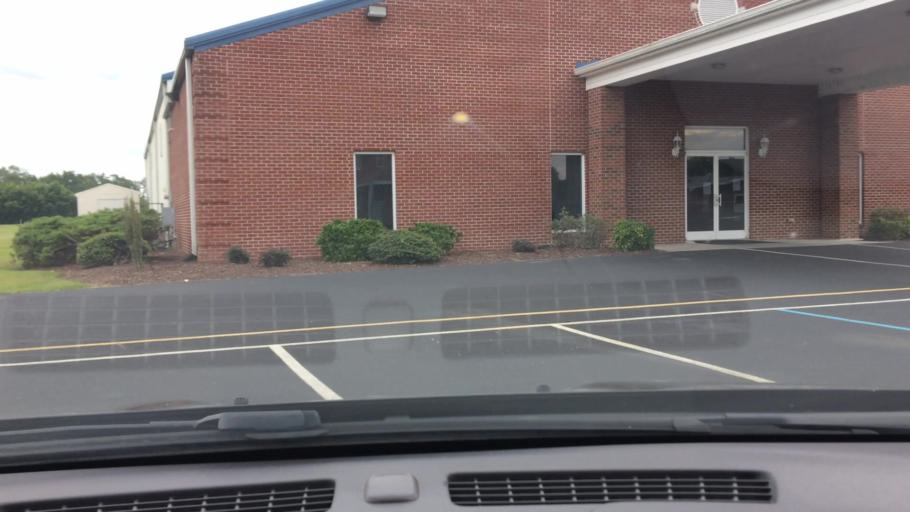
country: US
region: North Carolina
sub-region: Pitt County
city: Ayden
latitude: 35.4303
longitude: -77.4099
